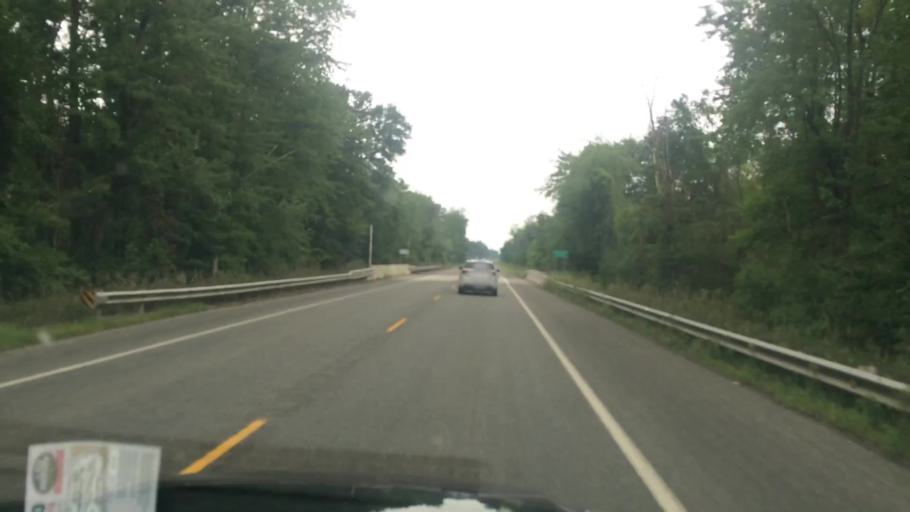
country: US
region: Michigan
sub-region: Tuscola County
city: Cass City
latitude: 43.6393
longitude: -83.0976
